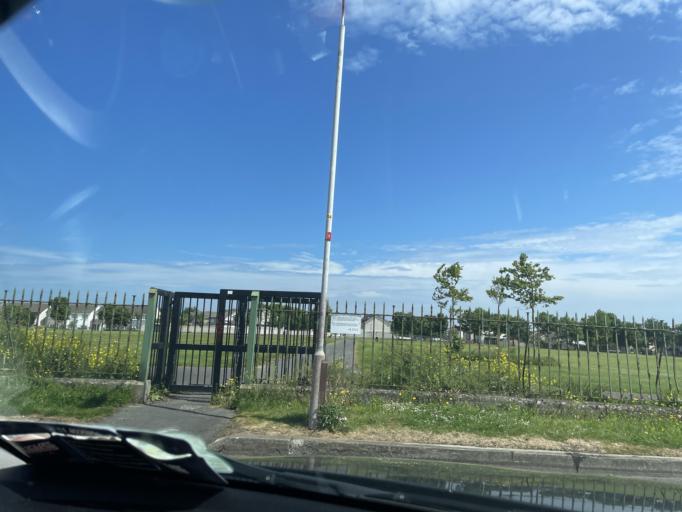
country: IE
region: Leinster
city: Raheny
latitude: 53.3957
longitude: -6.1745
